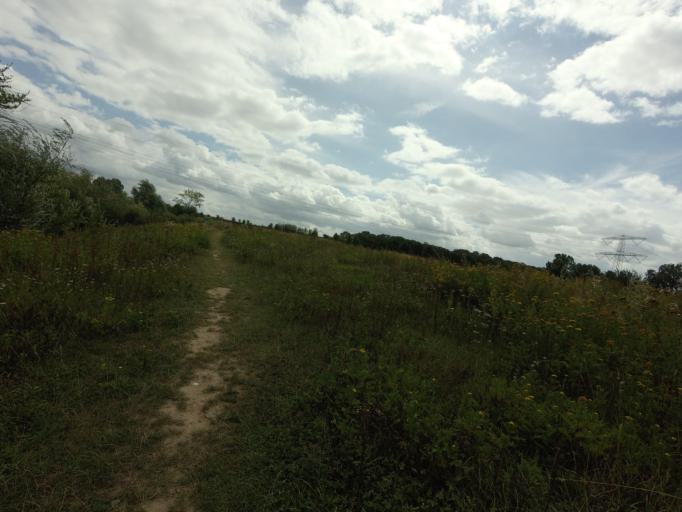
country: NL
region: Limburg
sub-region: Gemeente Maasgouw
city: Maasbracht
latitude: 51.1115
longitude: 5.8483
